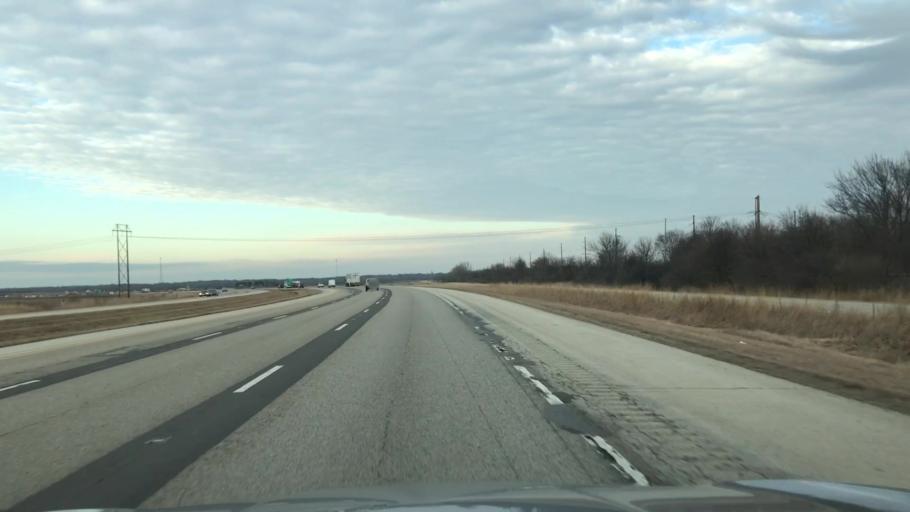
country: US
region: Illinois
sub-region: Logan County
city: Lincoln
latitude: 40.0975
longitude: -89.4188
